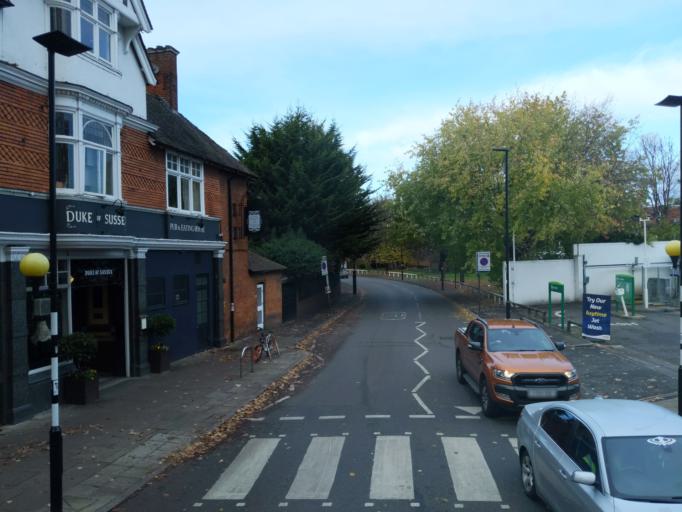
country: GB
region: England
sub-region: Greater London
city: Acton
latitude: 51.4962
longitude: -0.2639
